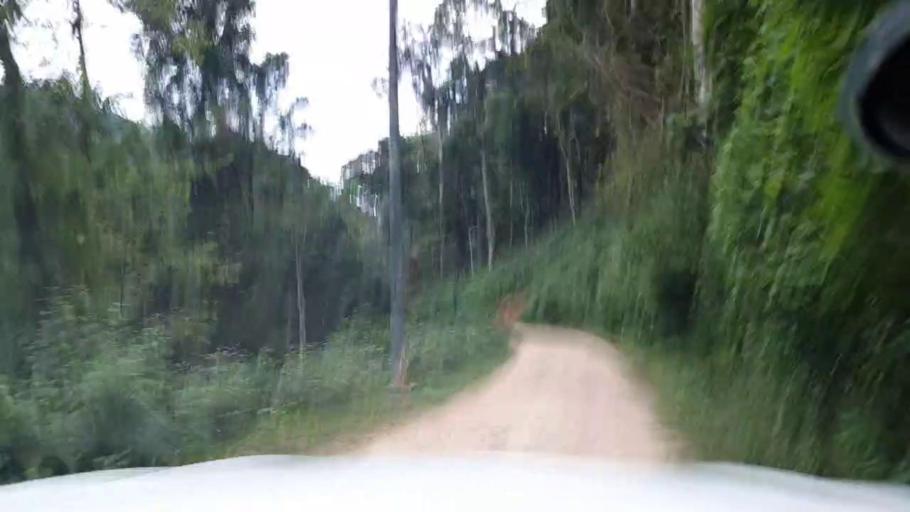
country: RW
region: Southern Province
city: Nzega
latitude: -2.5564
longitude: 29.2328
